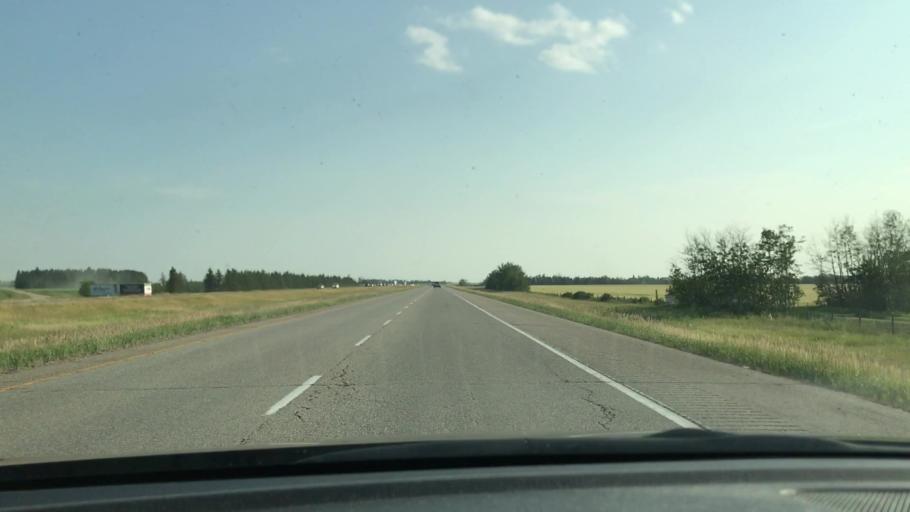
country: CA
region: Alberta
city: Leduc
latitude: 53.2147
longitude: -113.5858
